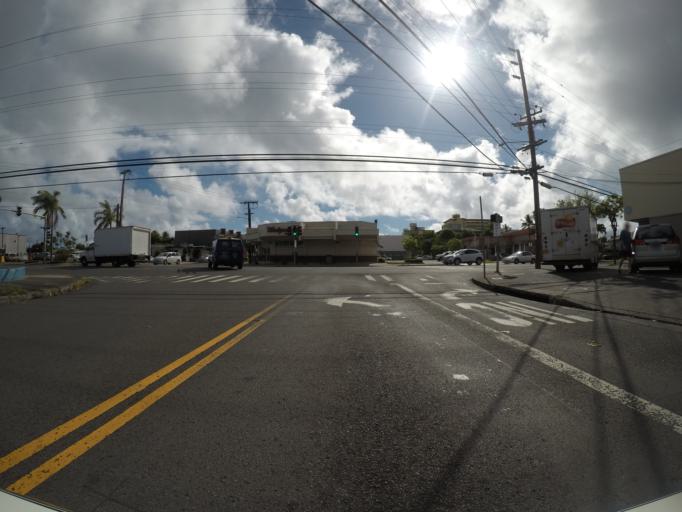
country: US
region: Hawaii
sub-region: Honolulu County
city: Kailua
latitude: 21.3956
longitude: -157.7449
